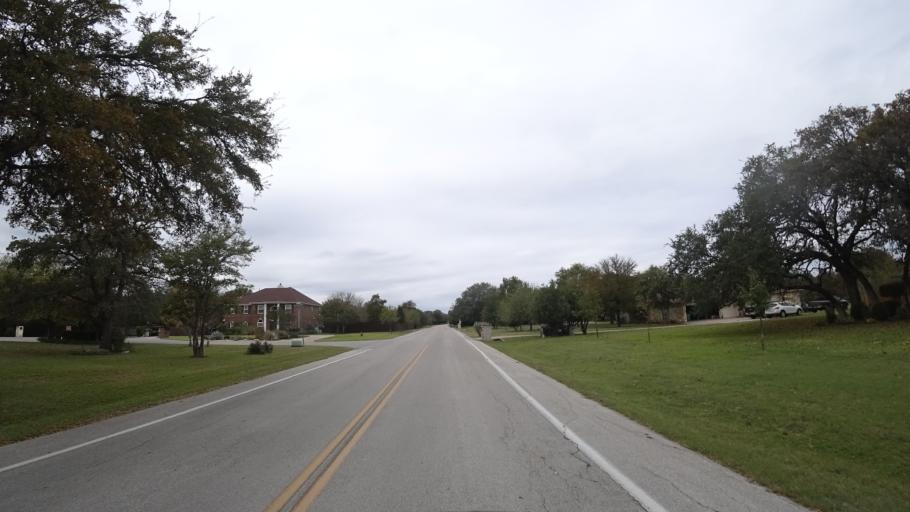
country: US
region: Texas
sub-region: Travis County
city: Shady Hollow
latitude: 30.1563
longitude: -97.8710
